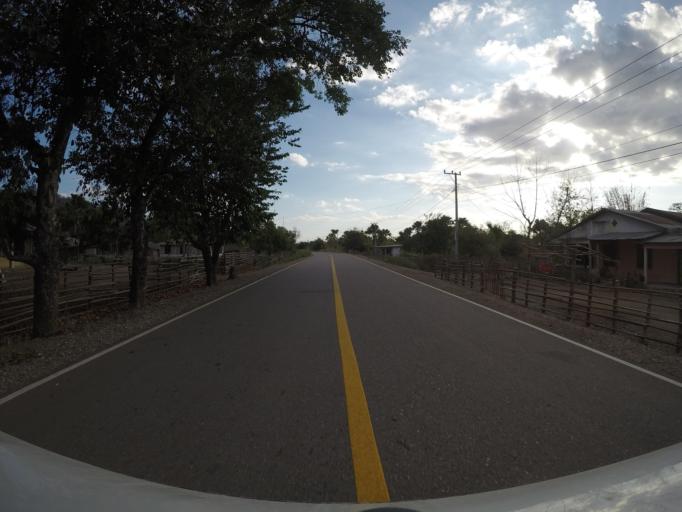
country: TL
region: Bobonaro
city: Maliana
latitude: -8.8822
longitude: 125.0296
